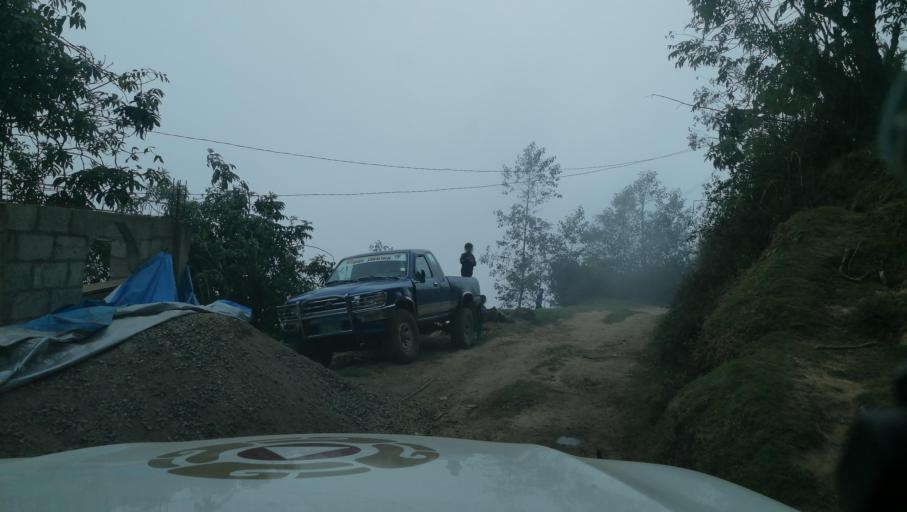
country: GT
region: San Marcos
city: Tacana
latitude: 15.2180
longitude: -92.1847
